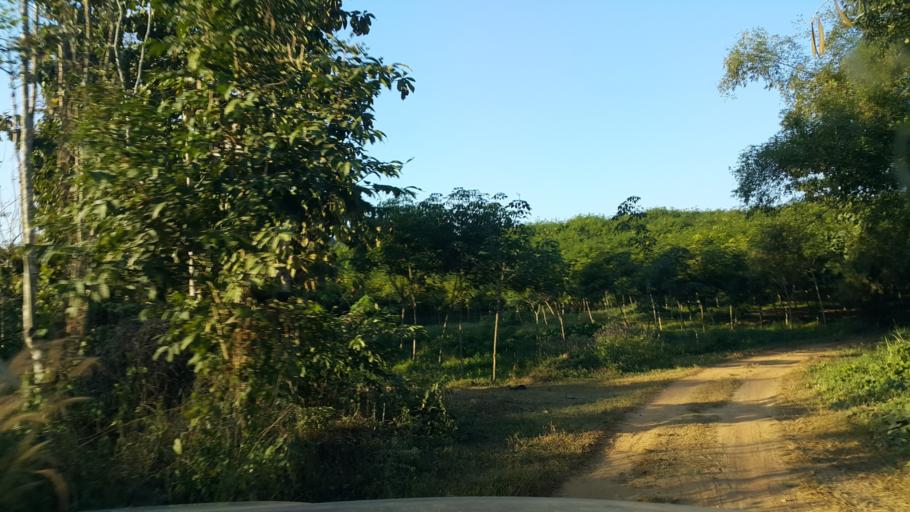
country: TH
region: Sukhothai
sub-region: Amphoe Si Satchanalai
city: Si Satchanalai
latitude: 17.5859
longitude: 99.6097
